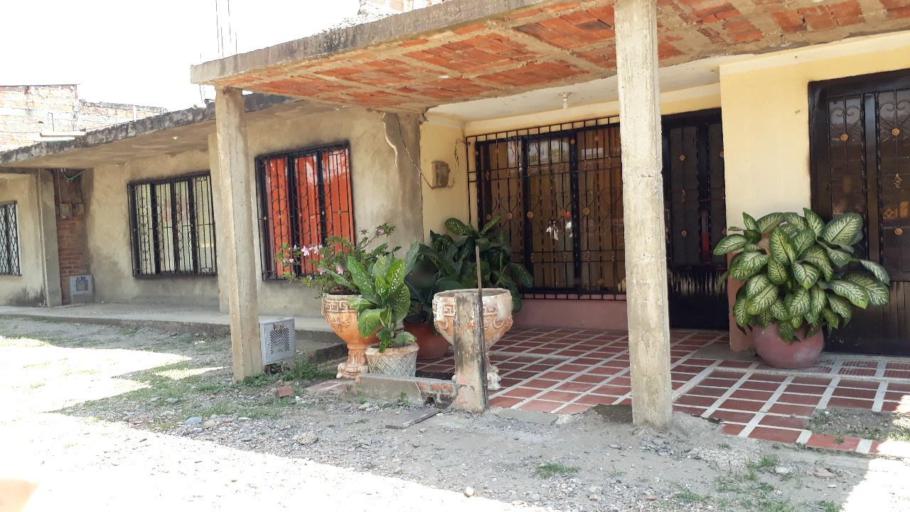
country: CO
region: Valle del Cauca
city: Jamundi
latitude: 3.1362
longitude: -76.5434
